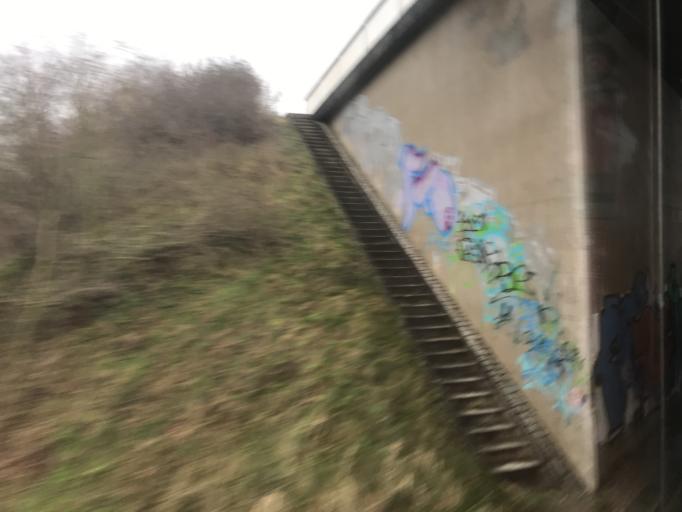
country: DE
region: Lower Saxony
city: Leiferde
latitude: 52.4567
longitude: 10.4689
